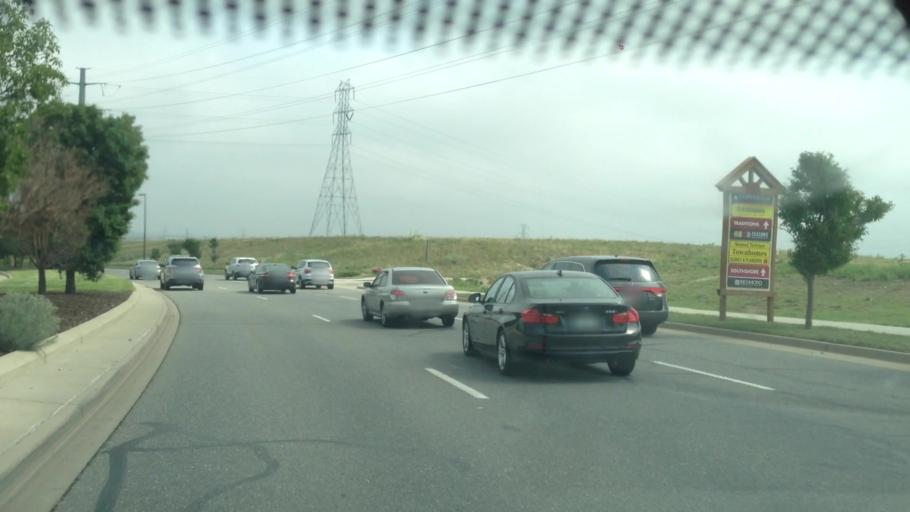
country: US
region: Colorado
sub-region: Douglas County
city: Parker
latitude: 39.6004
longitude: -104.7032
